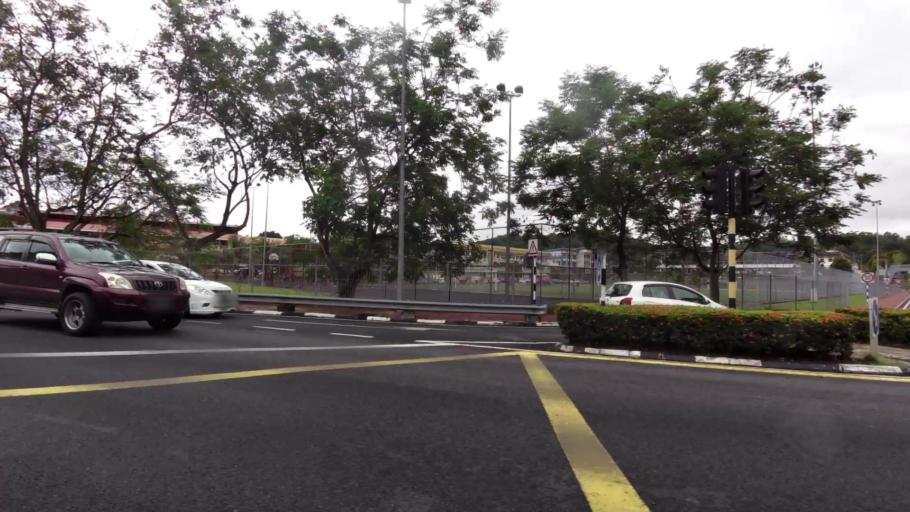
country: BN
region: Brunei and Muara
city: Bandar Seri Begawan
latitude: 4.9003
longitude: 114.9364
